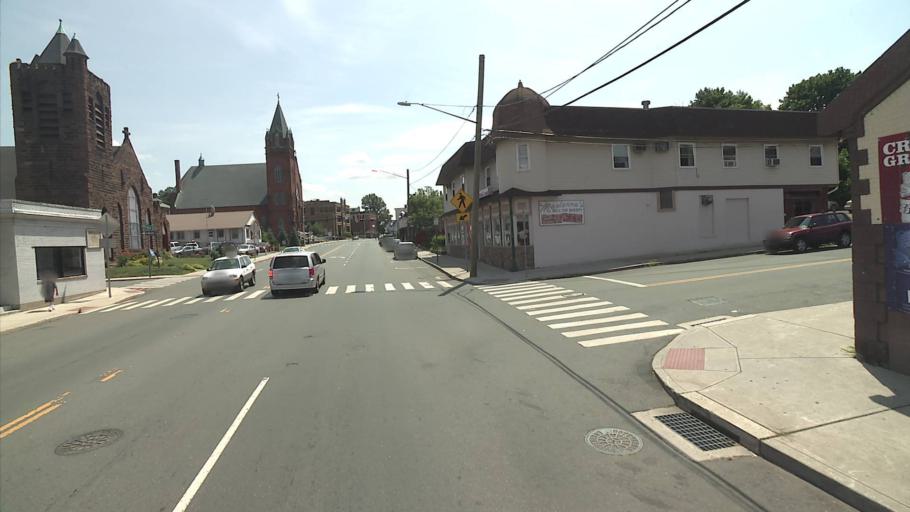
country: US
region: Connecticut
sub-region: New Haven County
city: Meriden
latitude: 41.5390
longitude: -72.8104
